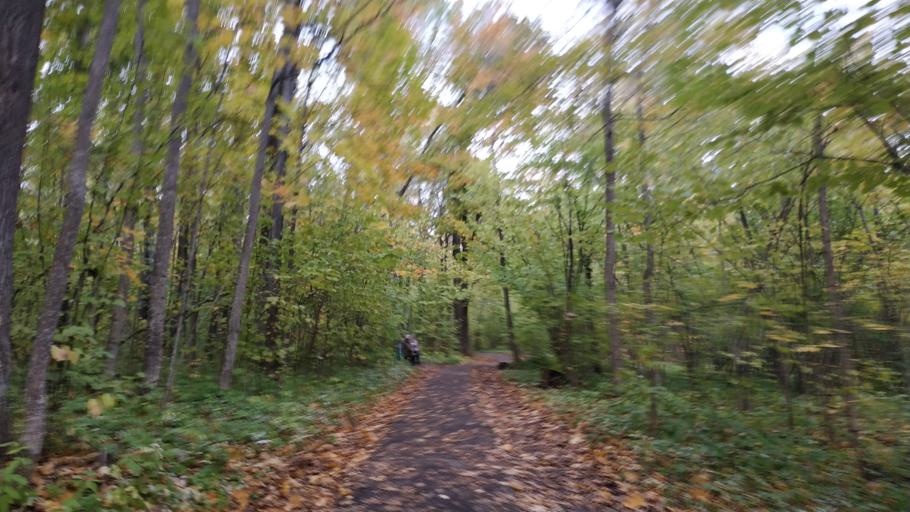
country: RU
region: Chuvashia
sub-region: Cheboksarskiy Rayon
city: Cheboksary
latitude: 56.1368
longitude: 47.1766
